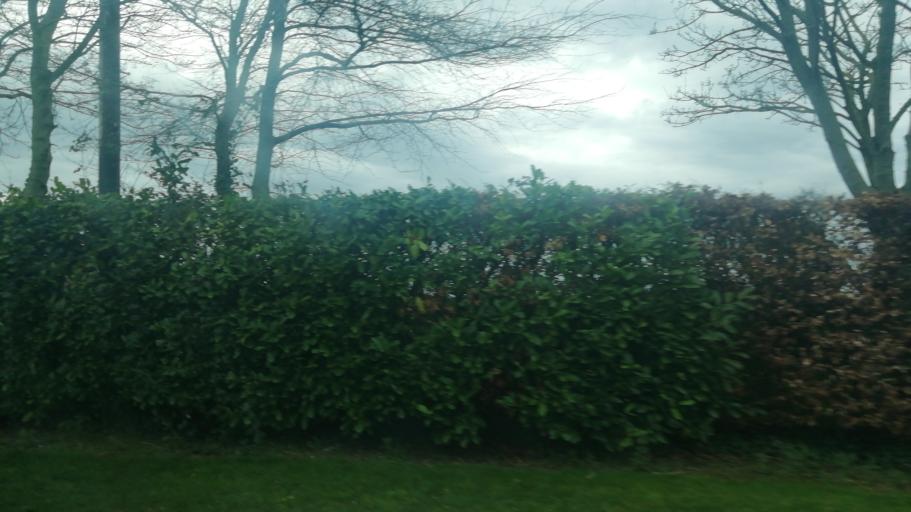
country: IE
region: Leinster
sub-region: Kildare
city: Clane
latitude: 53.3377
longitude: -6.6623
